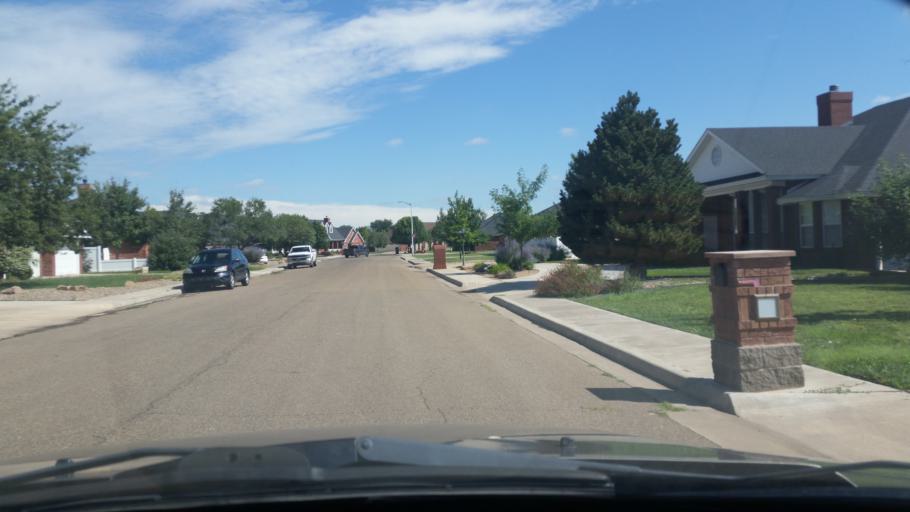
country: US
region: New Mexico
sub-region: Curry County
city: Clovis
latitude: 34.4381
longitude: -103.1777
